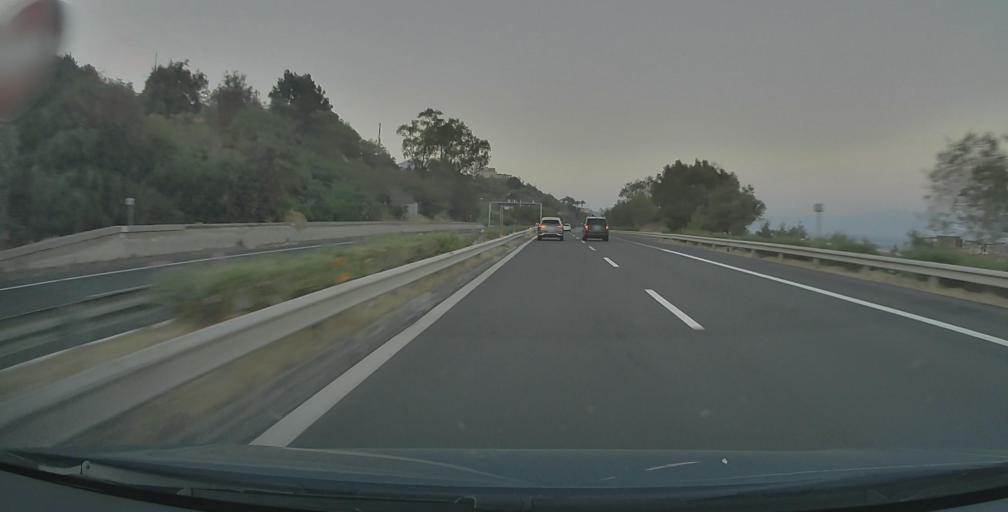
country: IT
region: Sicily
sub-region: Messina
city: Roccalumera
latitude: 37.9745
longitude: 15.3916
